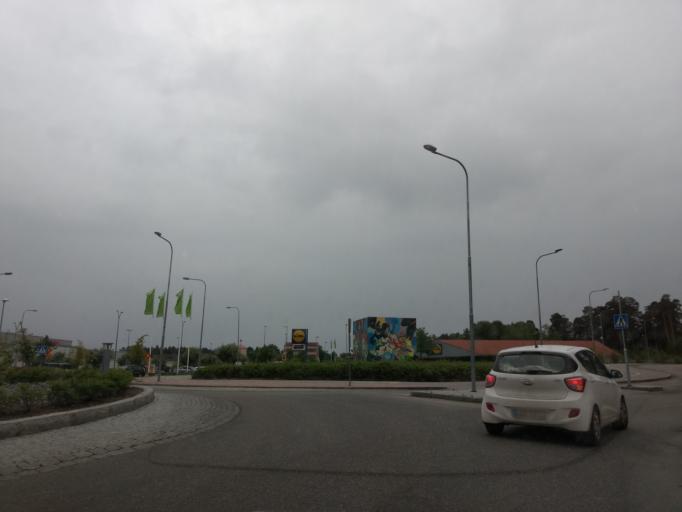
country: SE
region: Uppsala
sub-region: Uppsala Kommun
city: Uppsala
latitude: 59.8118
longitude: 17.6261
